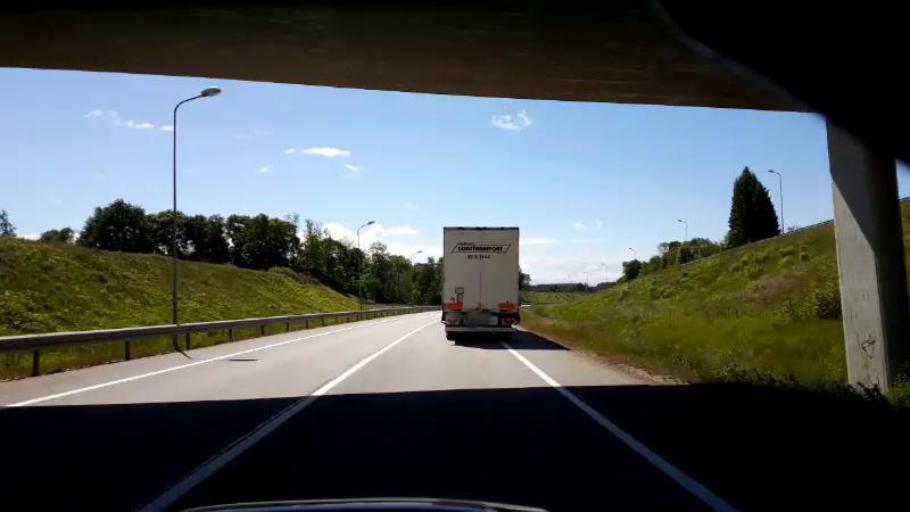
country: LV
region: Saulkrastu
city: Saulkrasti
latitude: 57.3274
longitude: 24.4561
